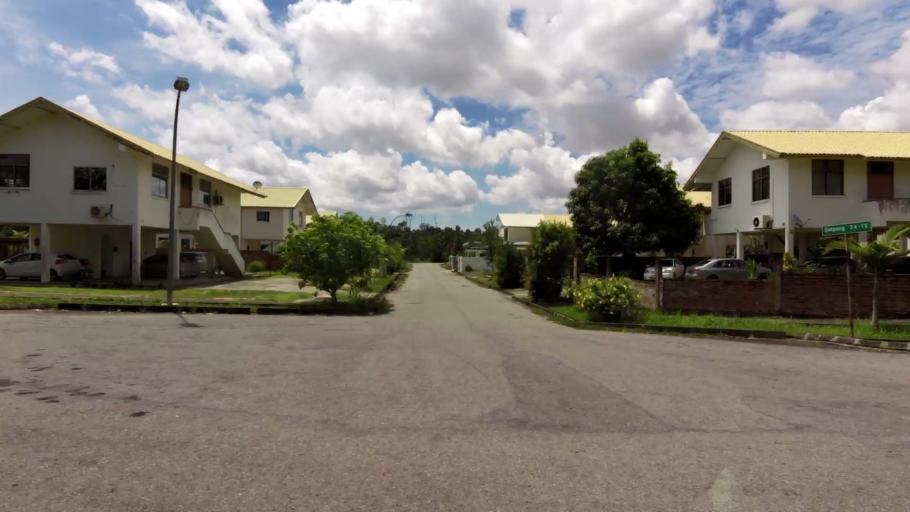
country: BN
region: Brunei and Muara
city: Bandar Seri Begawan
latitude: 4.9586
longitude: 114.9023
